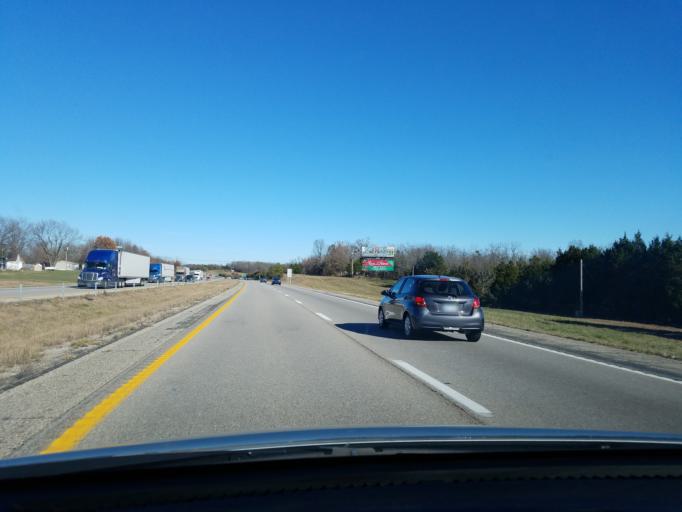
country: US
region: Missouri
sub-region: Laclede County
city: Lebanon
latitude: 37.6041
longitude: -92.7076
